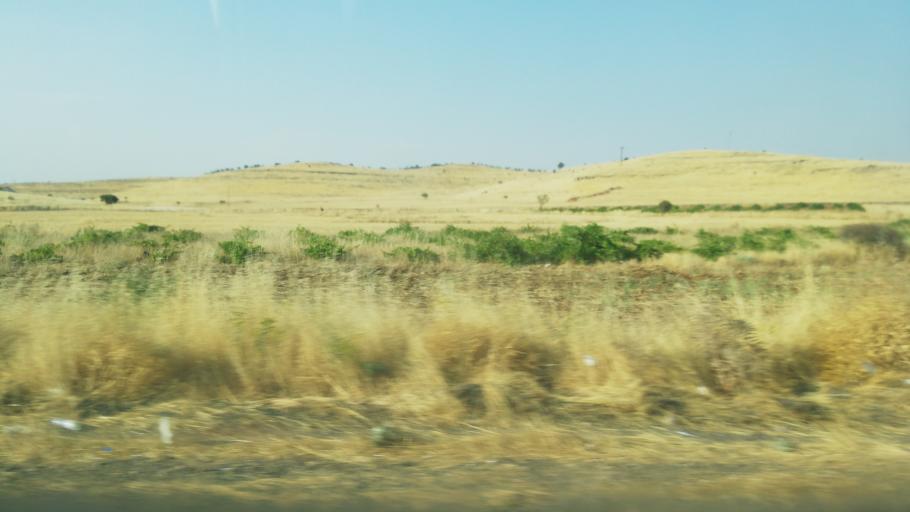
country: TR
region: Mardin
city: Kindirip
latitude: 37.4534
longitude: 41.2543
